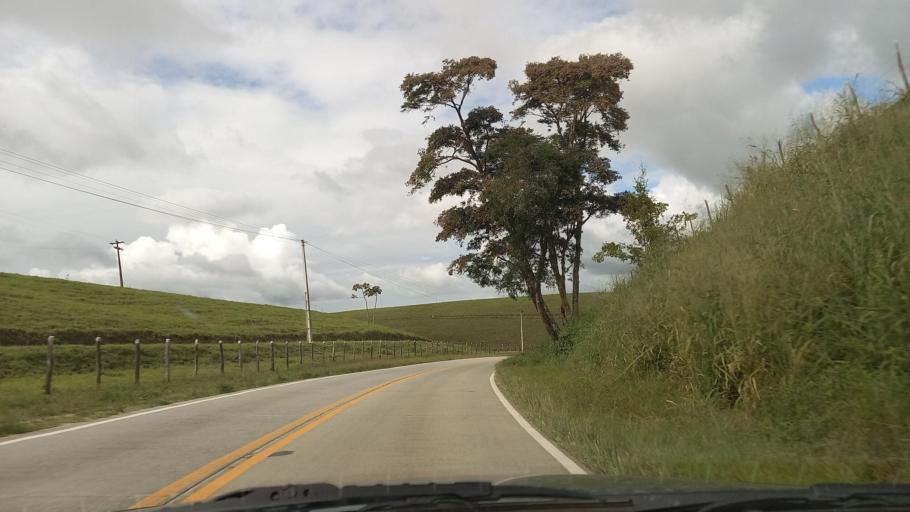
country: BR
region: Pernambuco
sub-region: Quipapa
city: Quipapa
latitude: -8.7758
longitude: -35.9305
